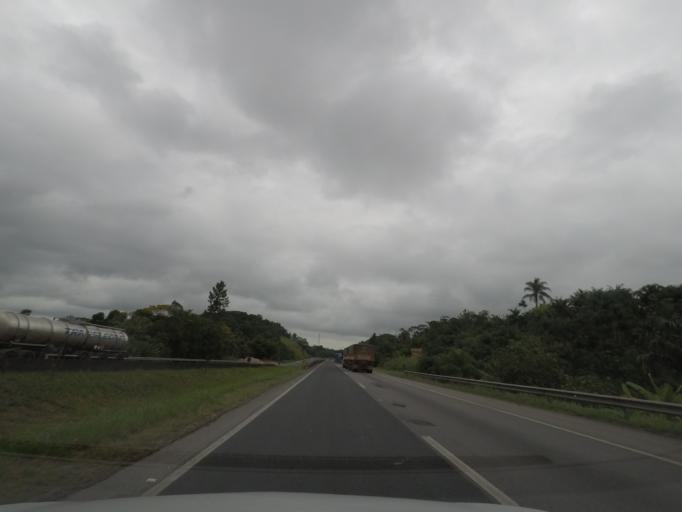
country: BR
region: Sao Paulo
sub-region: Juquia
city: Juquia
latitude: -24.3999
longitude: -47.7359
